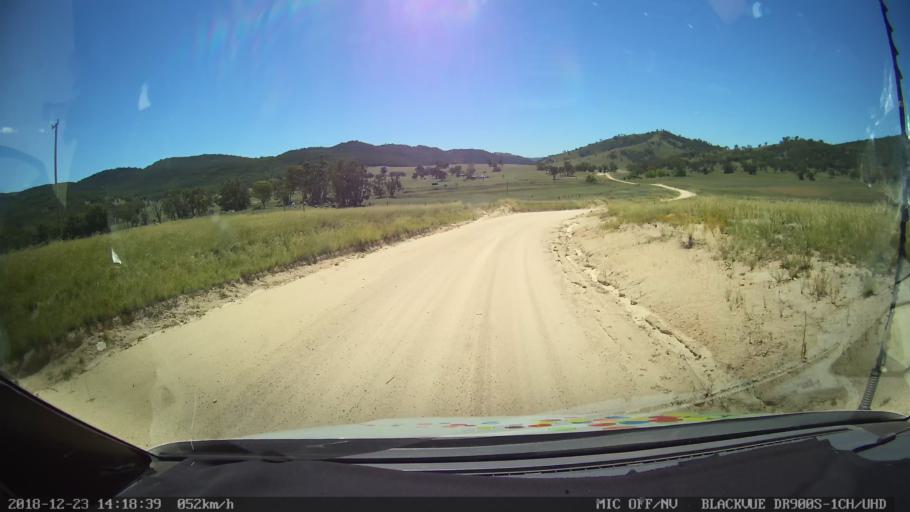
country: AU
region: New South Wales
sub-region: Tamworth Municipality
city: Manilla
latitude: -30.6570
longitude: 151.0017
